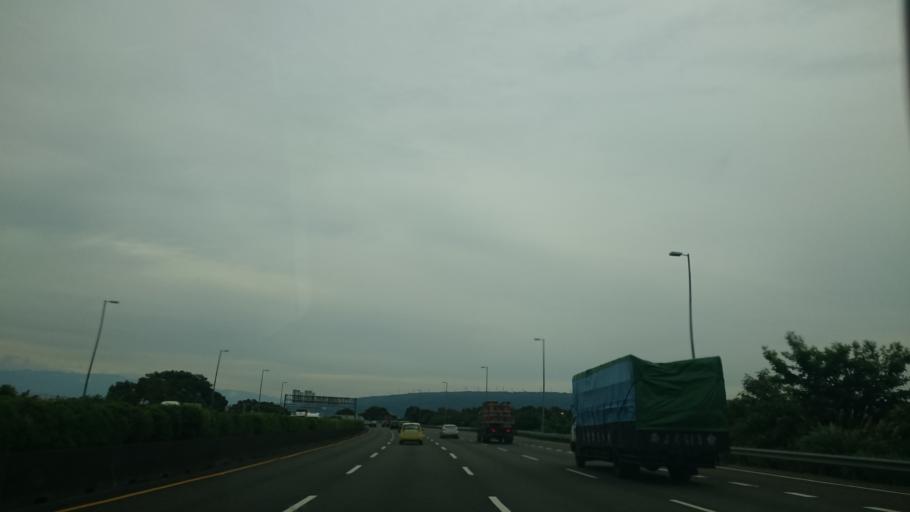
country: TW
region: Taiwan
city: Zhongxing New Village
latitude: 24.0003
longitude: 120.6503
